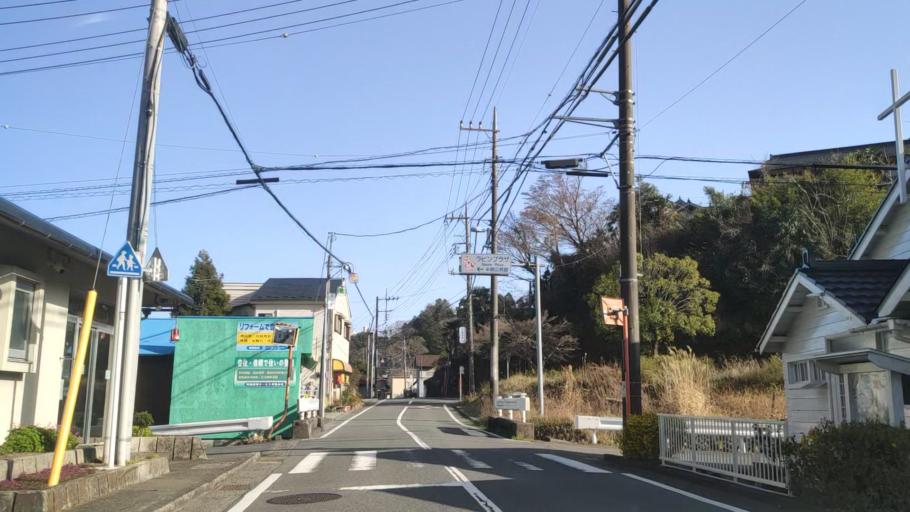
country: JP
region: Tokyo
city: Hachioji
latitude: 35.5449
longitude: 139.2673
